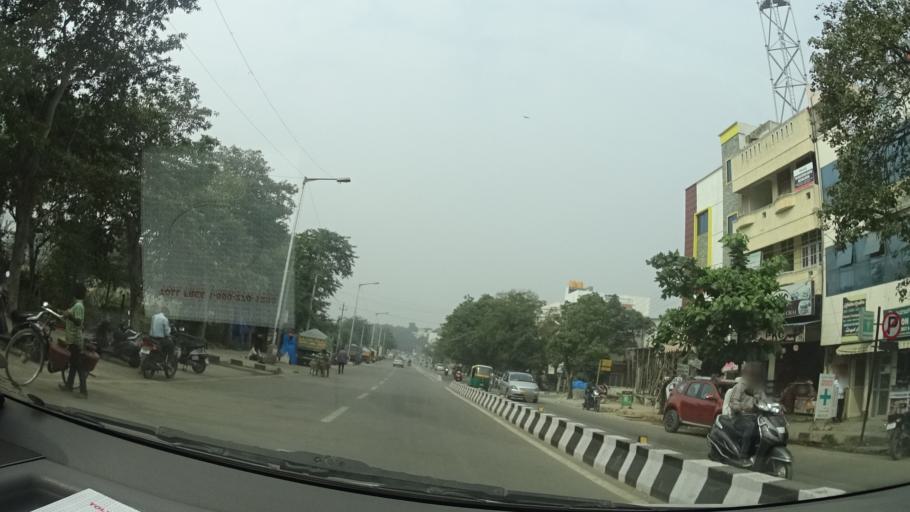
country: IN
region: Karnataka
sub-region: Bangalore Urban
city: Bangalore
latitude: 13.0211
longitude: 77.6285
